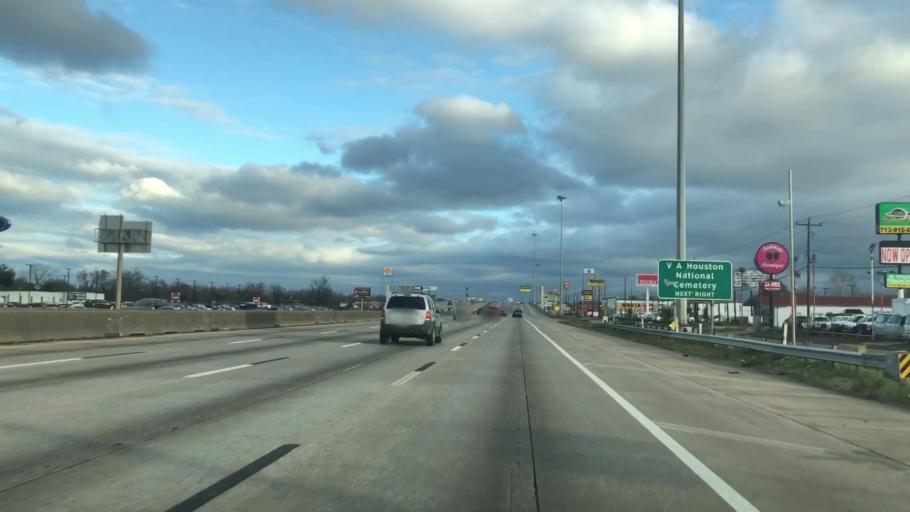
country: US
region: Texas
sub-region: Harris County
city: Aldine
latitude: 29.8937
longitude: -95.4118
